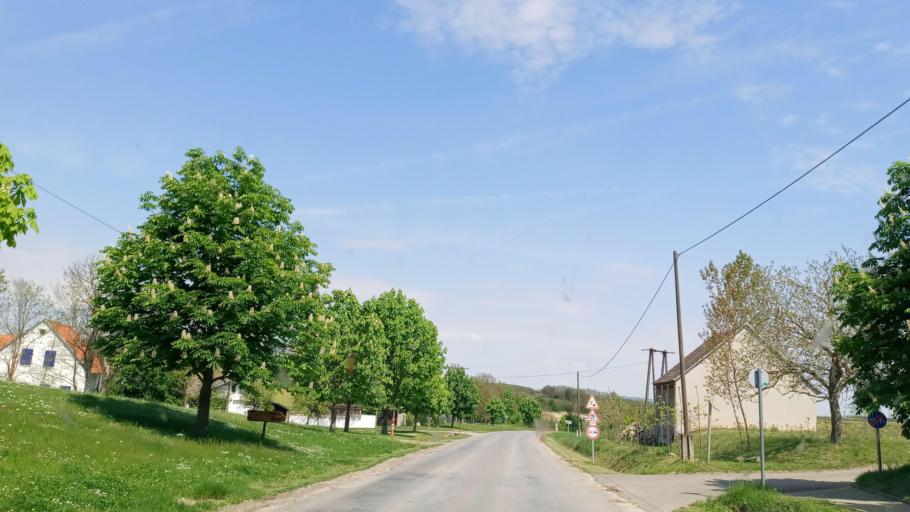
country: HU
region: Baranya
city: Boly
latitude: 45.9194
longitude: 18.5442
